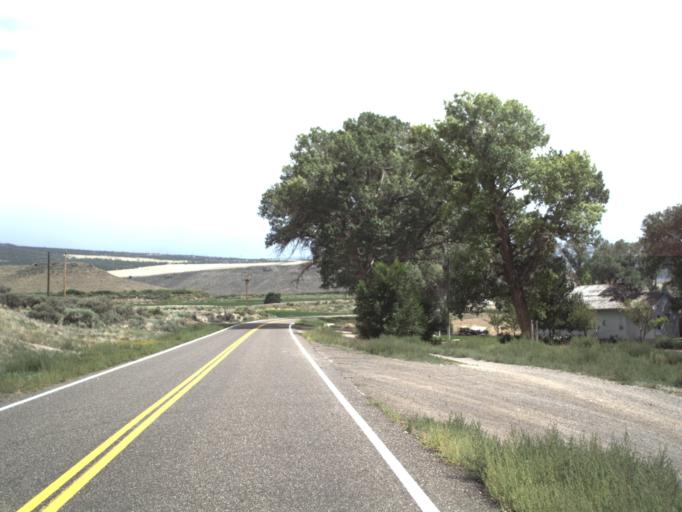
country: US
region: Utah
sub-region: Piute County
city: Junction
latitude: 38.1555
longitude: -112.0049
